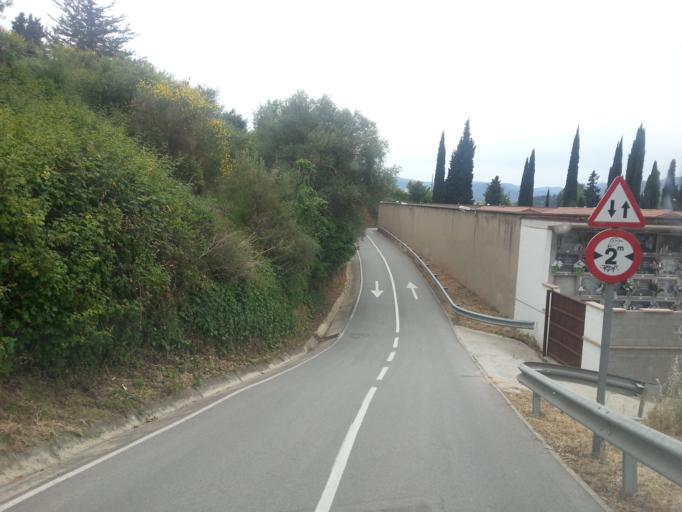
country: ES
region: Catalonia
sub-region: Provincia de Barcelona
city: Molins de Rei
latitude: 41.4209
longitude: 2.0200
